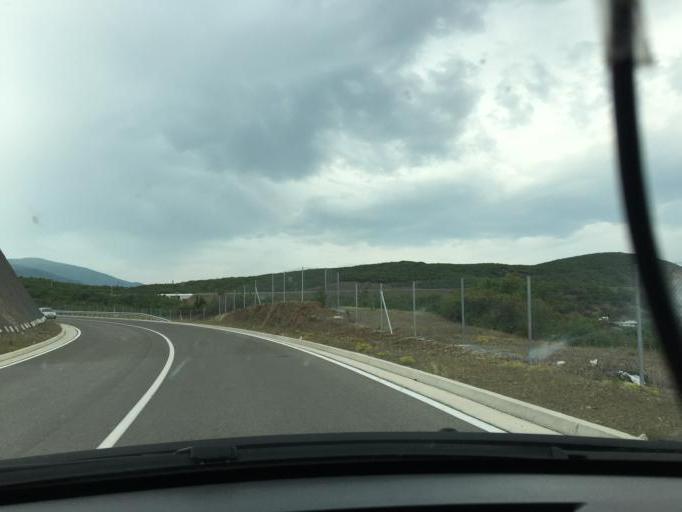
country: MK
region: Gevgelija
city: Miravci
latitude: 41.3021
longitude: 22.4348
